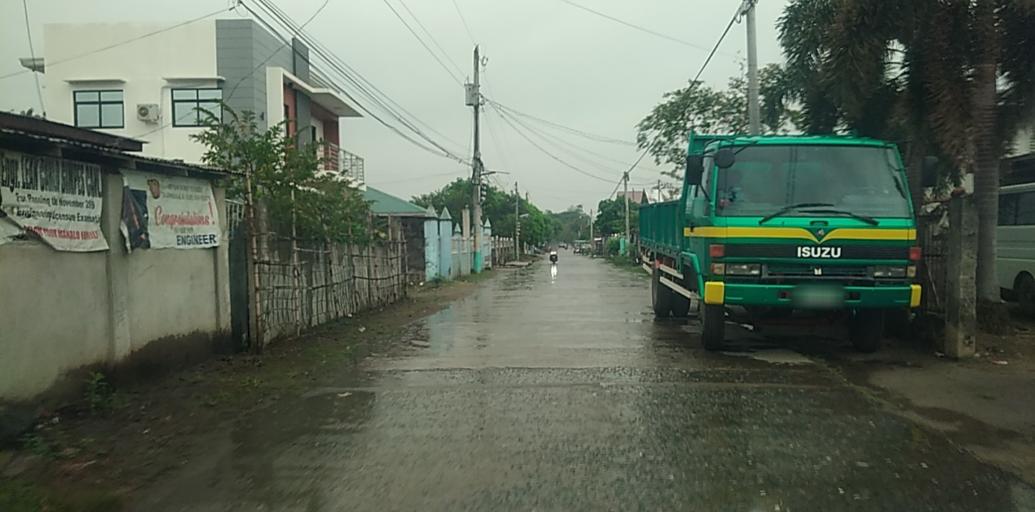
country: PH
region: Central Luzon
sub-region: Province of Pampanga
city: Arenas
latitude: 15.1754
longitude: 120.6818
